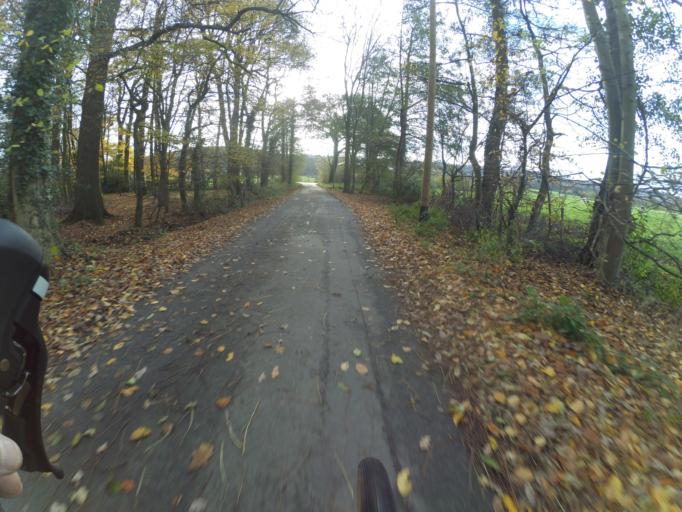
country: DE
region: North Rhine-Westphalia
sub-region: Regierungsbezirk Munster
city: Tecklenburg
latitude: 52.2367
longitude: 7.8019
